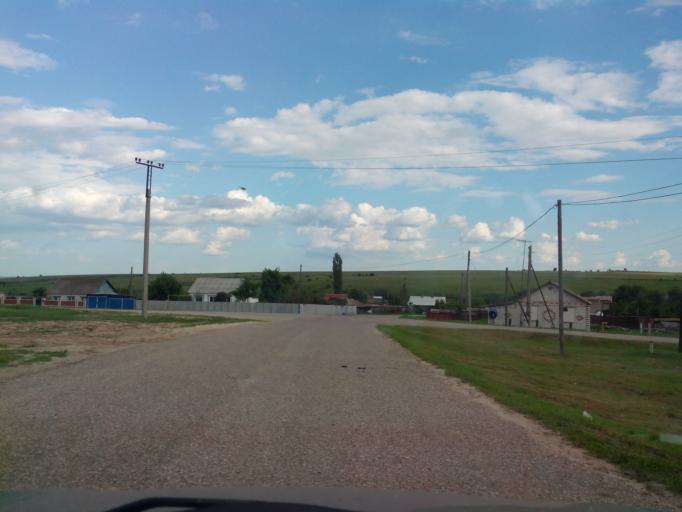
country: RU
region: Volgograd
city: Slashchevskaya
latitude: 49.7781
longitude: 42.4407
